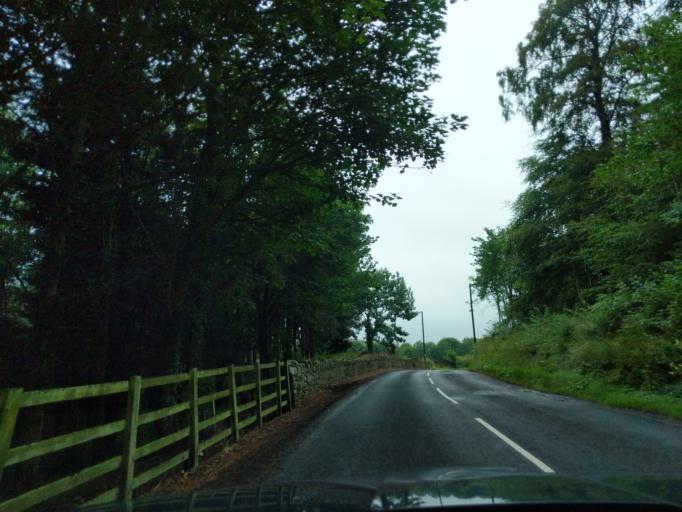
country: GB
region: England
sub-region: Northumberland
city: Ford
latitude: 55.6516
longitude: -2.1154
